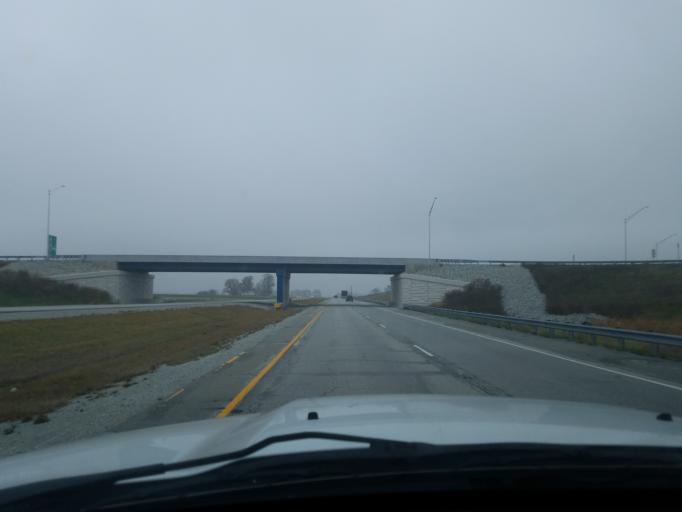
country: US
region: Indiana
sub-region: Tipton County
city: Tipton
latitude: 40.2749
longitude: -86.1270
